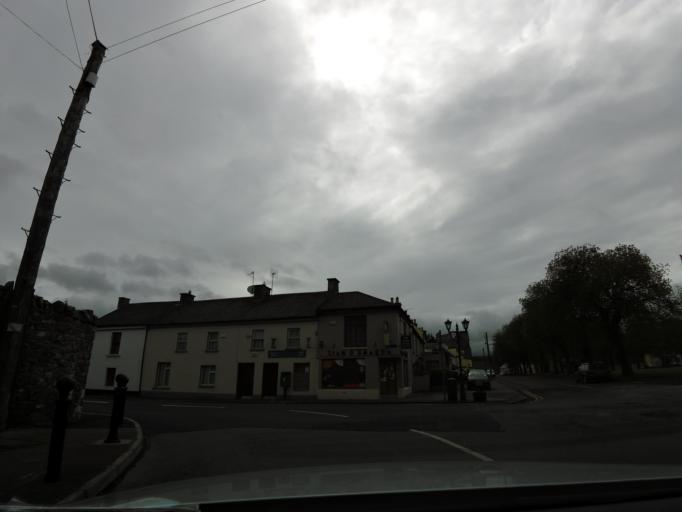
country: IE
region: Leinster
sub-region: Kilkenny
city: Ballyragget
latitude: 52.7326
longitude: -7.3981
